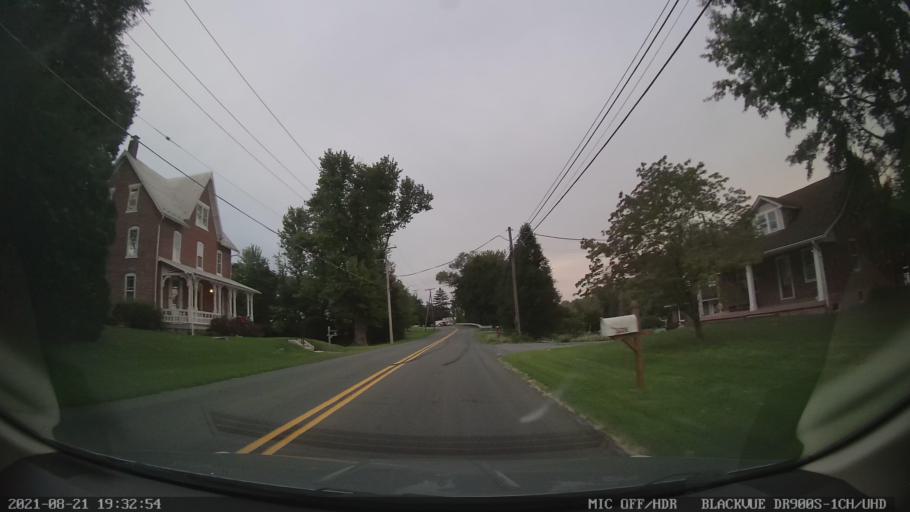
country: US
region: Pennsylvania
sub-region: Berks County
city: Oley
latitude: 40.3958
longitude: -75.7983
